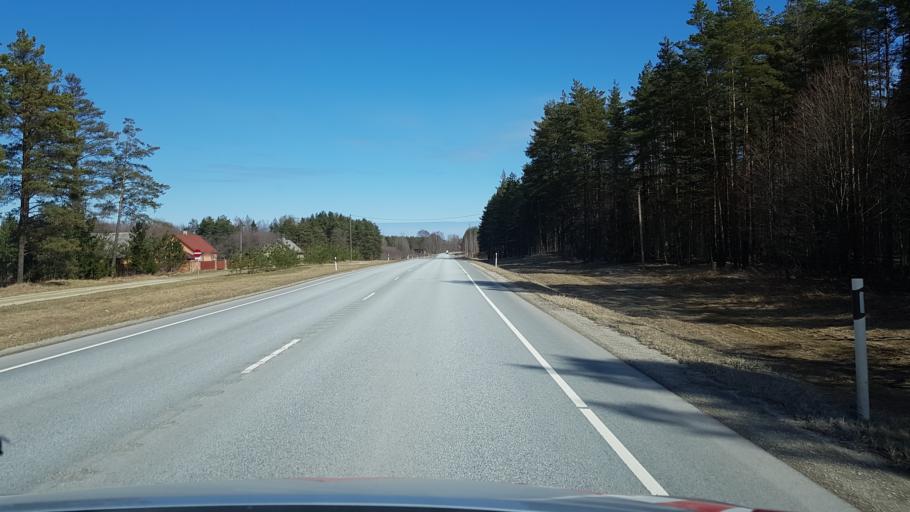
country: EE
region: Laeaene-Virumaa
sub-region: Viru-Nigula vald
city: Kunda
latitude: 59.4018
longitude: 26.6319
